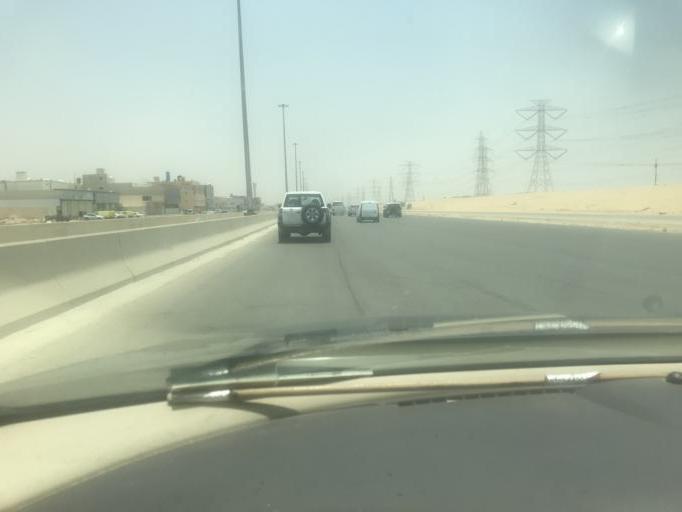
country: SA
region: Ar Riyad
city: Riyadh
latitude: 24.8188
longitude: 46.7374
